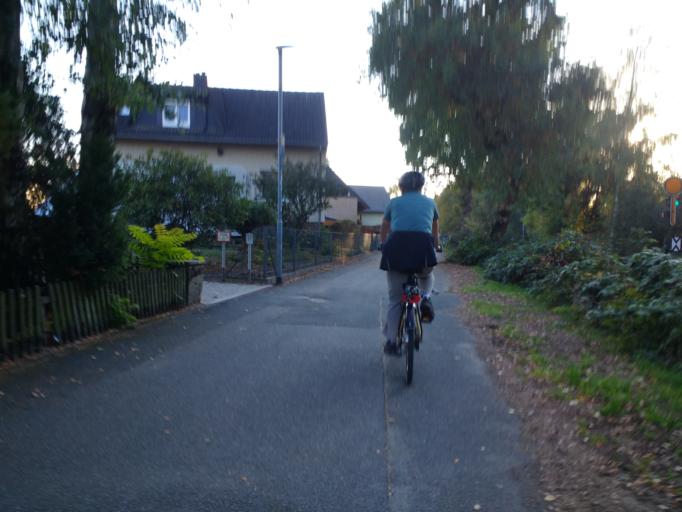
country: DE
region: Lower Saxony
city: Gifhorn
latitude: 52.4864
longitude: 10.5592
